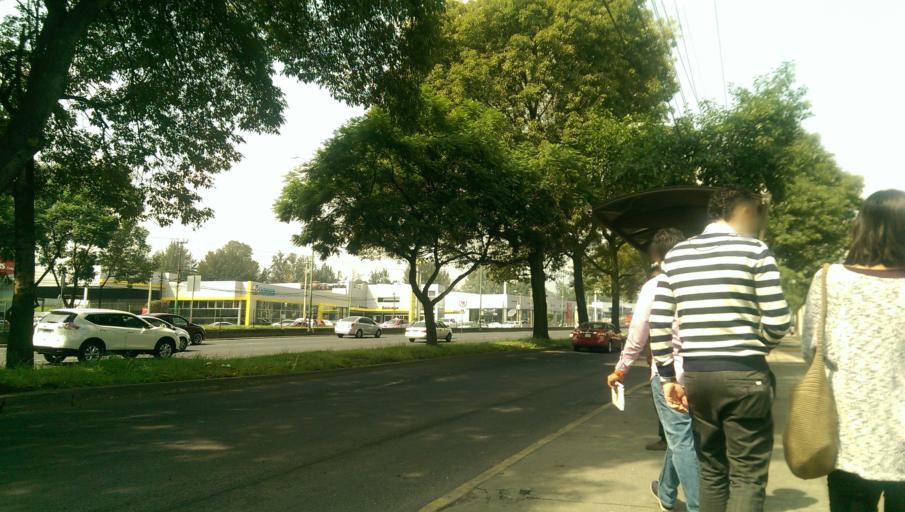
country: MX
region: Mexico City
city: Tlalpan
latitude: 19.2828
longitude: -99.1348
